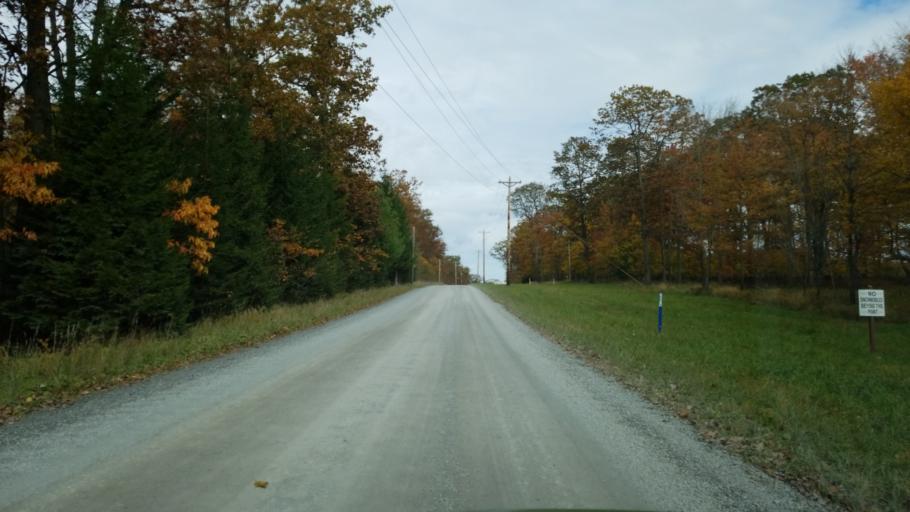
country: US
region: Pennsylvania
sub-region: Clearfield County
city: Clearfield
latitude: 41.1482
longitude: -78.4681
